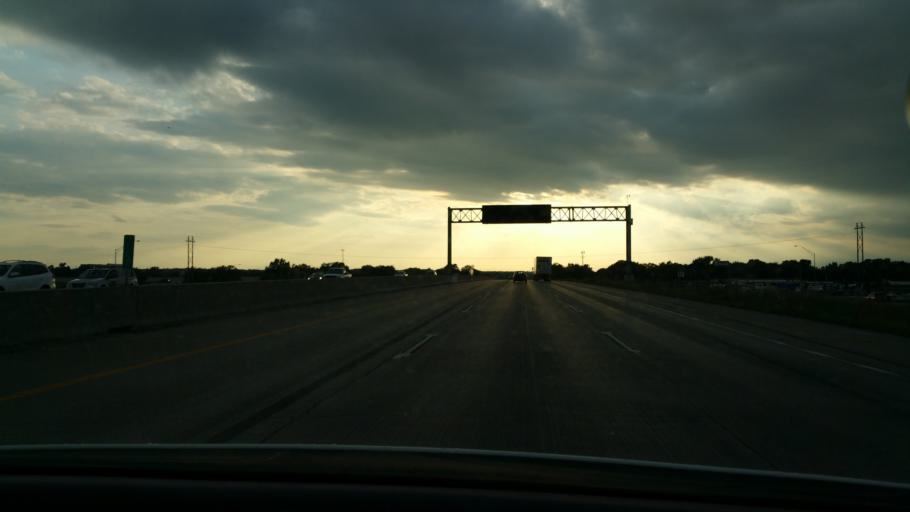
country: US
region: Iowa
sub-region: Polk County
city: Saylorville
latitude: 41.6495
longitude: -93.6159
